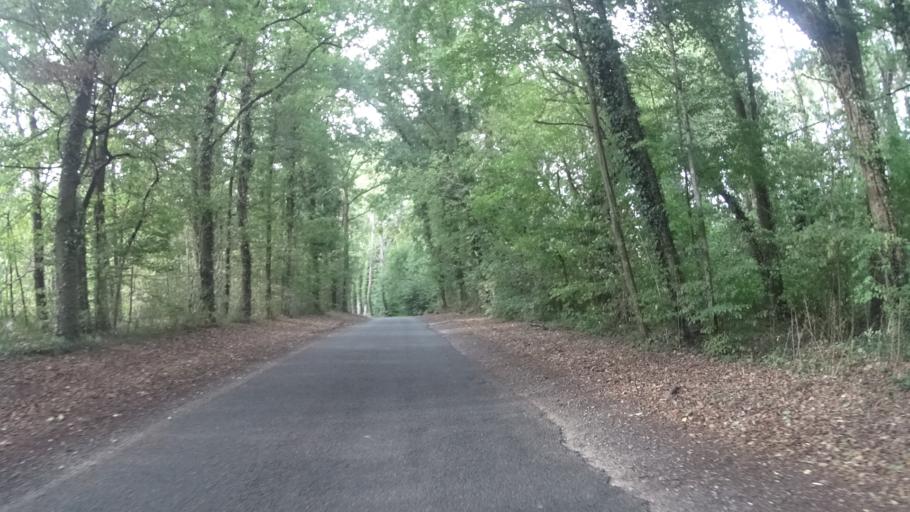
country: FR
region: Picardie
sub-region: Departement de l'Oise
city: Ver-sur-Launette
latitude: 49.1691
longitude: 2.6801
